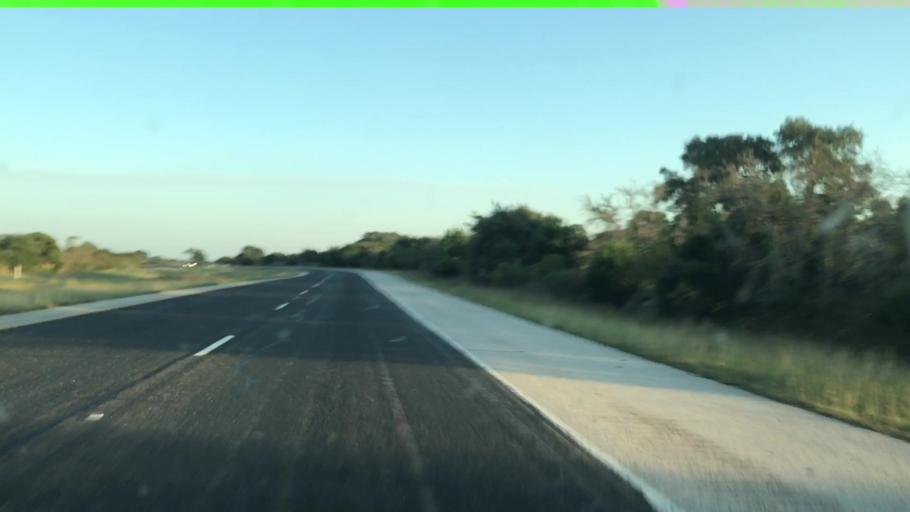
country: US
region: Texas
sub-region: Kerr County
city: Kerrville
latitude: 30.0615
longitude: -99.0497
